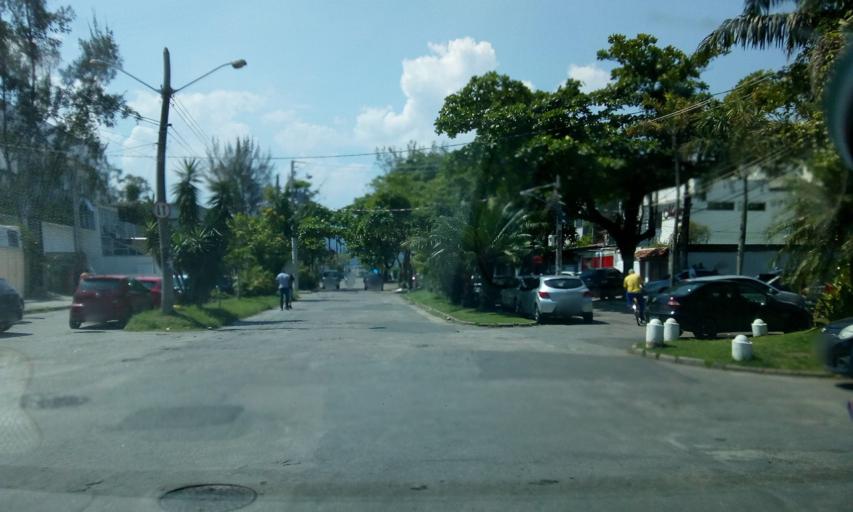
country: BR
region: Rio de Janeiro
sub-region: Nilopolis
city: Nilopolis
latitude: -23.0211
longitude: -43.4804
